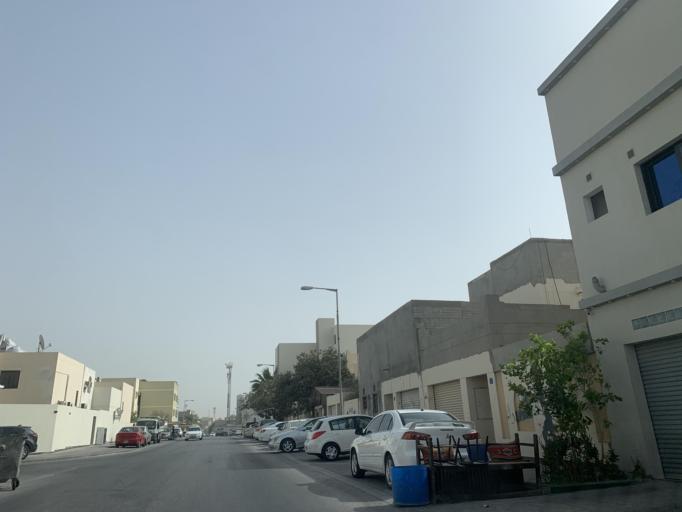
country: BH
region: Northern
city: Madinat `Isa
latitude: 26.1783
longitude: 50.5230
